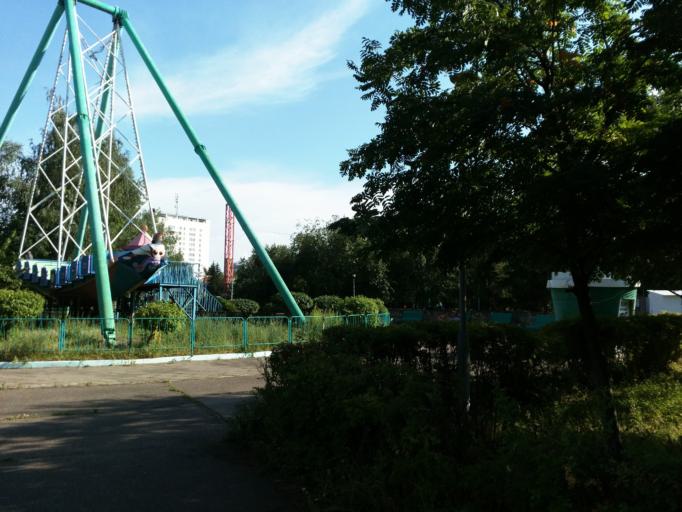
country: RU
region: Tatarstan
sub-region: Tukayevskiy Rayon
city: Naberezhnyye Chelny
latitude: 55.7557
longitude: 52.4257
